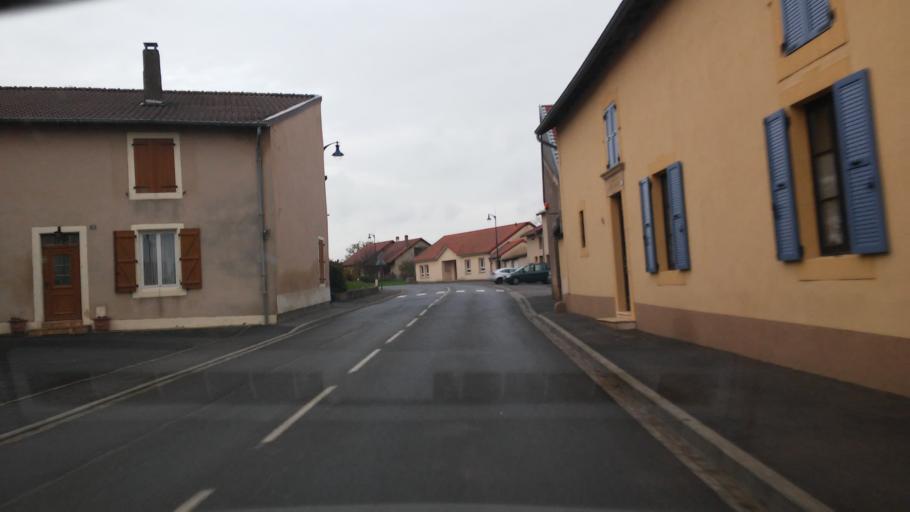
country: FR
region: Lorraine
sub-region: Departement de la Moselle
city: Ennery
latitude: 49.2081
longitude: 6.2347
